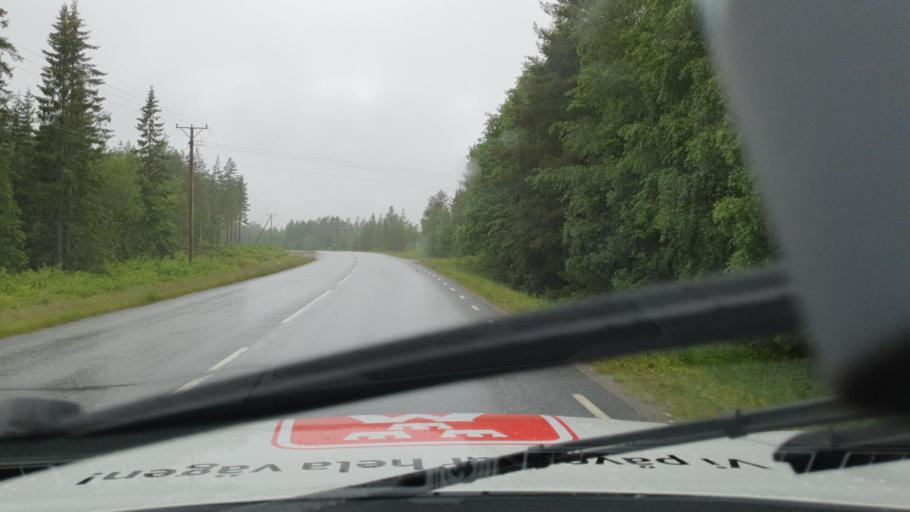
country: SE
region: Vaesterbotten
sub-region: Umea Kommun
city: Roback
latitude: 63.7740
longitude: 20.0298
